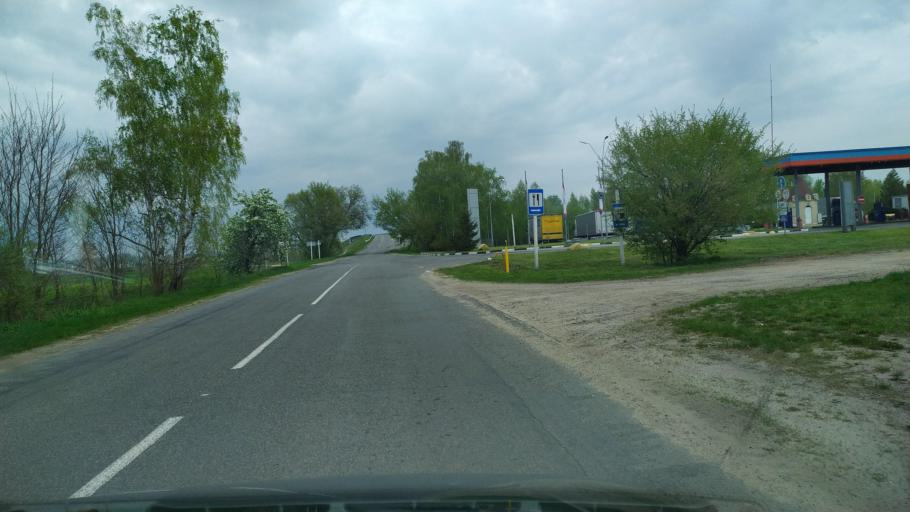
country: BY
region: Brest
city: Zhabinka
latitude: 52.1584
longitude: 24.0849
